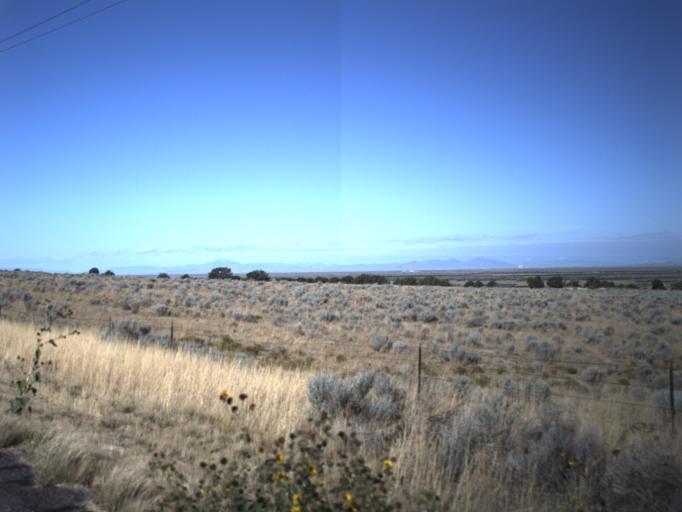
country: US
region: Utah
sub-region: Millard County
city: Delta
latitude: 39.4551
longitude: -112.3011
